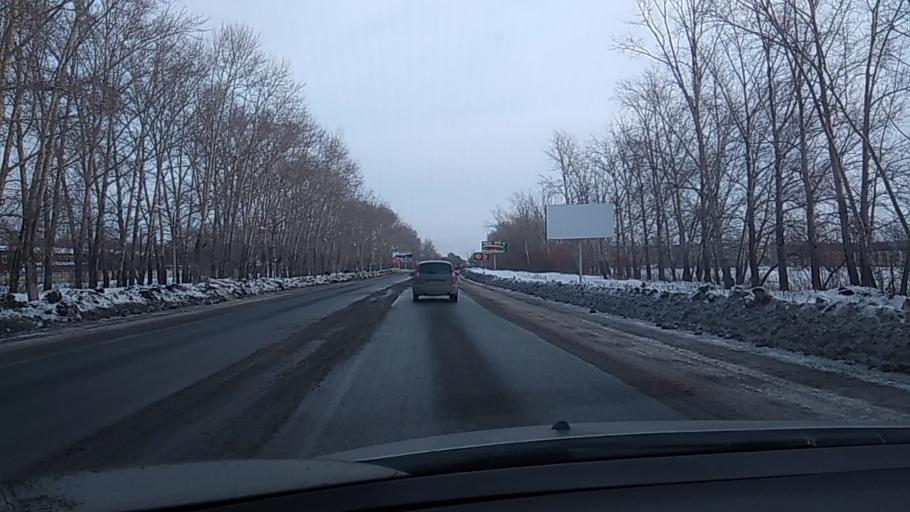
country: RU
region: Sverdlovsk
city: Martyush
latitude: 56.4387
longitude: 61.8387
